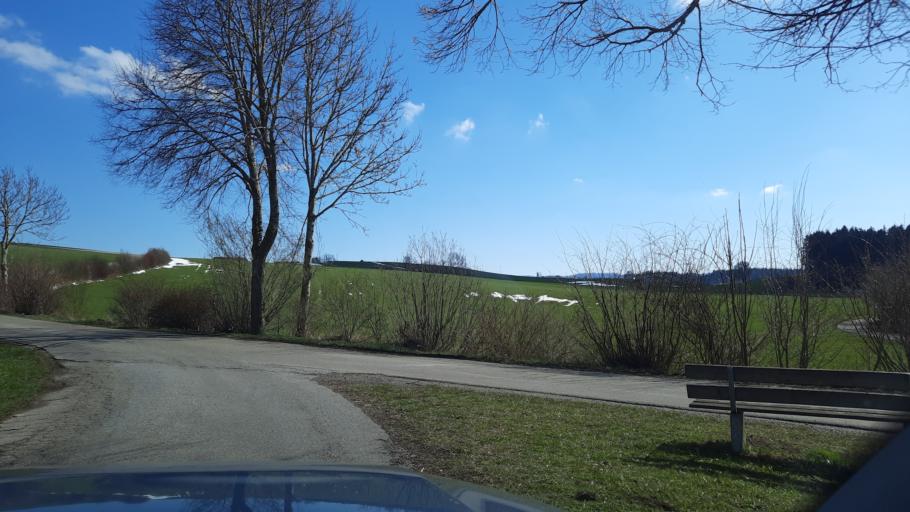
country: DE
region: Bavaria
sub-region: Swabia
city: Altusried
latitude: 47.8194
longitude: 10.1979
